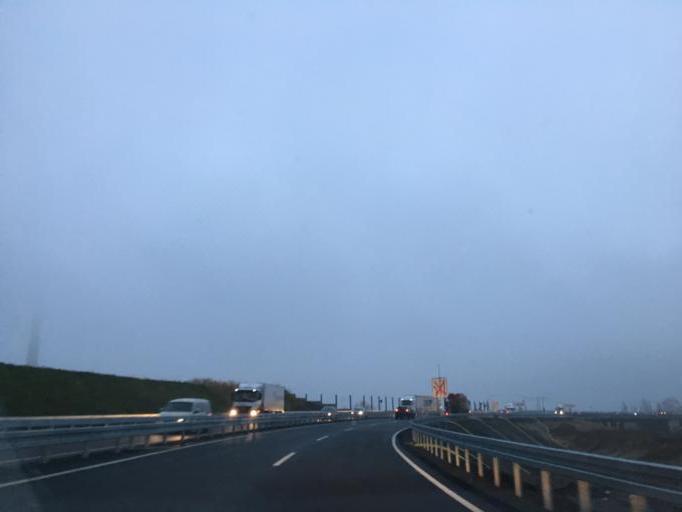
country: DE
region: Saxony
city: Borna
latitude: 51.1402
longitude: 12.5059
